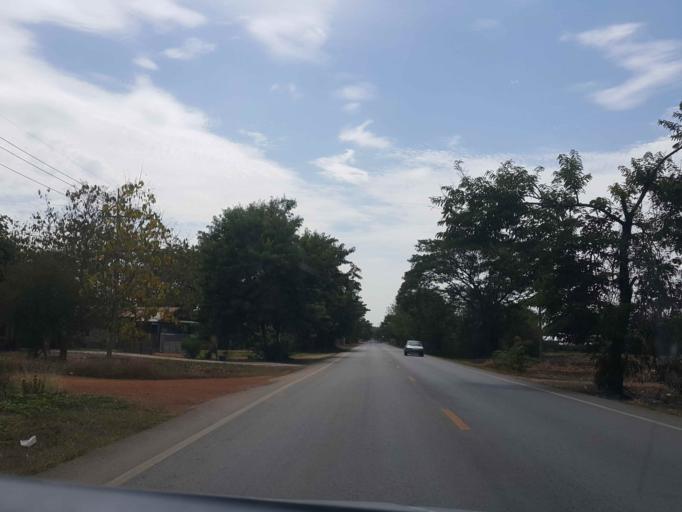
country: TH
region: Sukhothai
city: Thung Saliam
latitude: 17.3349
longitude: 99.5611
